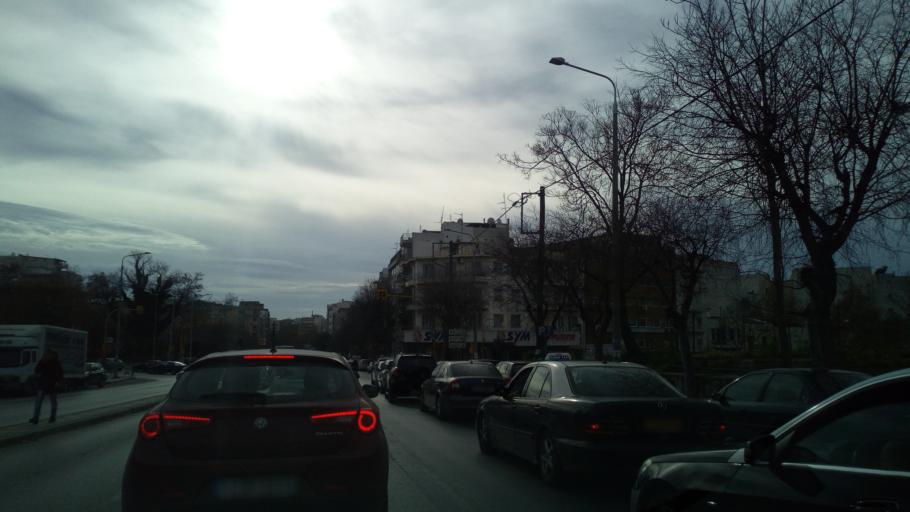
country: GR
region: Central Macedonia
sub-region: Nomos Thessalonikis
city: Thessaloniki
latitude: 40.6454
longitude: 22.9353
